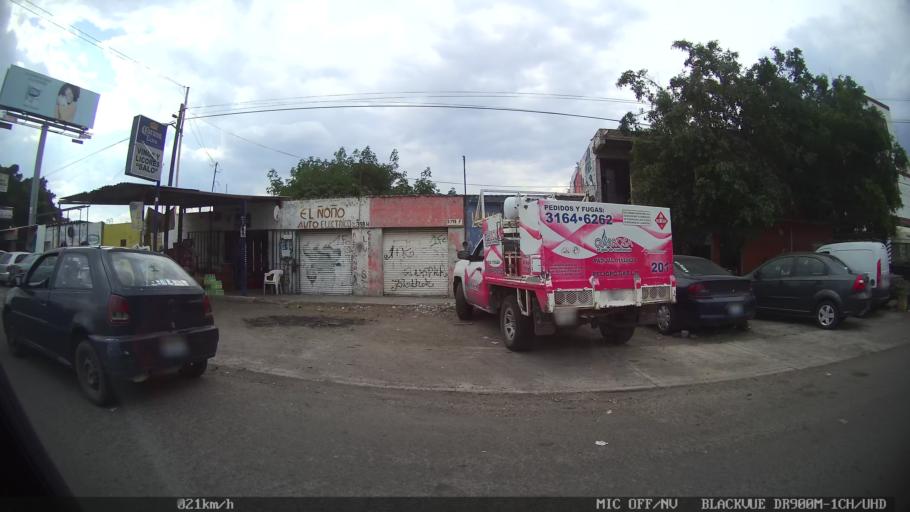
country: MX
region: Jalisco
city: Tlaquepaque
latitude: 20.6173
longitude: -103.2739
